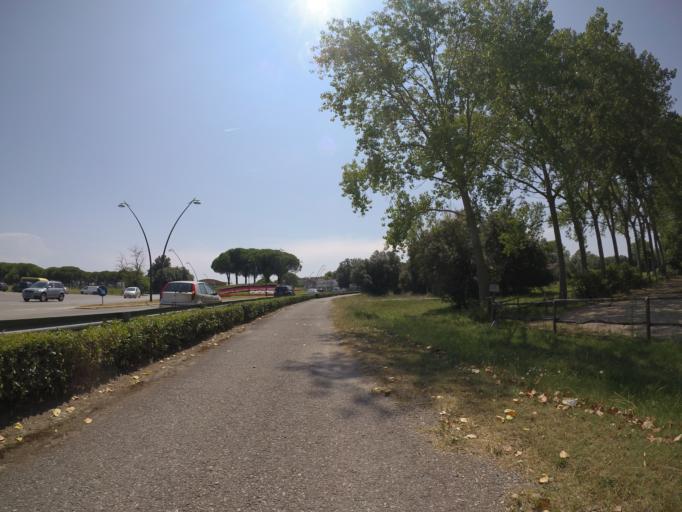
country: IT
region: Veneto
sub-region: Provincia di Venezia
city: Bibione
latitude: 45.6504
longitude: 13.0606
